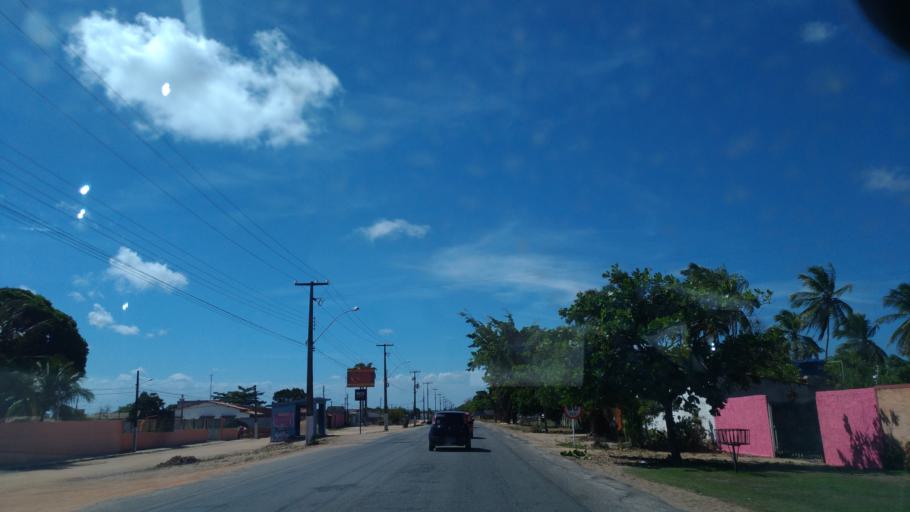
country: BR
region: Alagoas
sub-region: Marechal Deodoro
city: Marechal Deodoro
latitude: -9.7549
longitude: -35.8715
